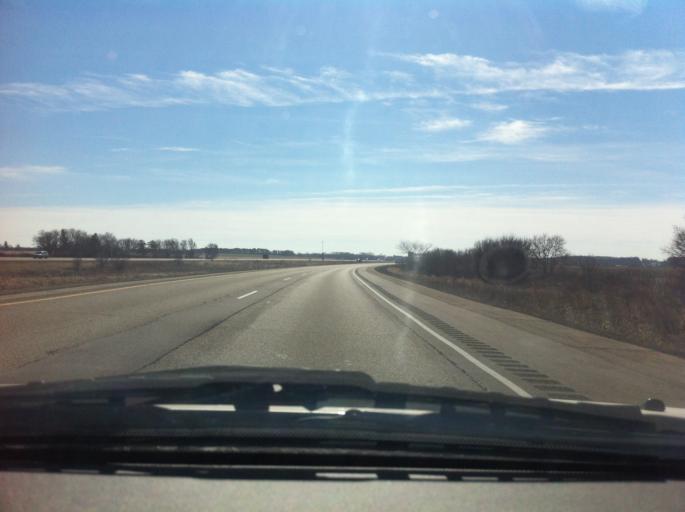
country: US
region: Wisconsin
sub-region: Rock County
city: Edgerton
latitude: 42.8410
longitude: -89.0301
